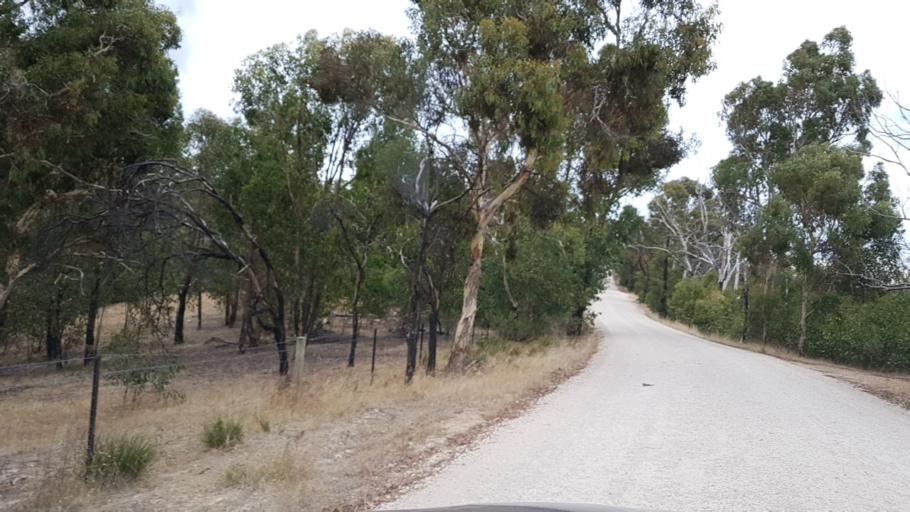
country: AU
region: South Australia
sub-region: Tea Tree Gully
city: Golden Grove
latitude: -34.7835
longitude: 138.8136
